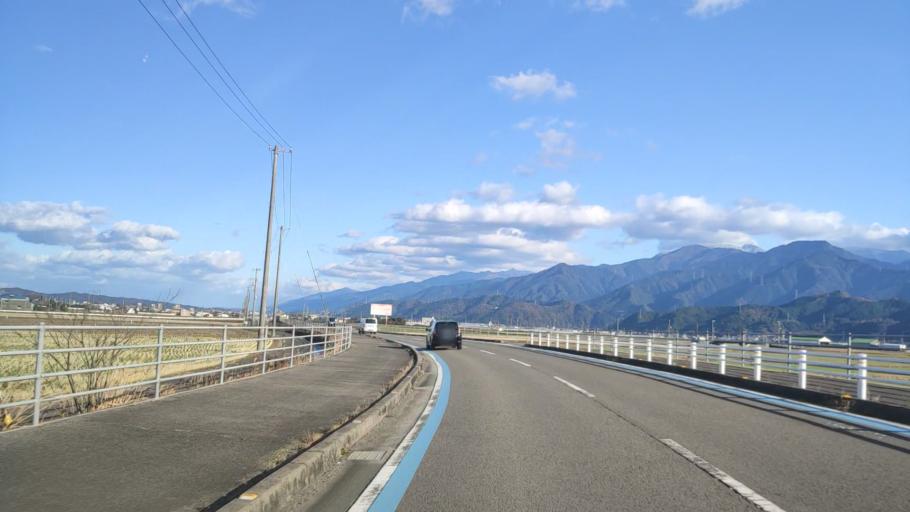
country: JP
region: Ehime
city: Saijo
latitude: 33.9071
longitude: 133.1442
